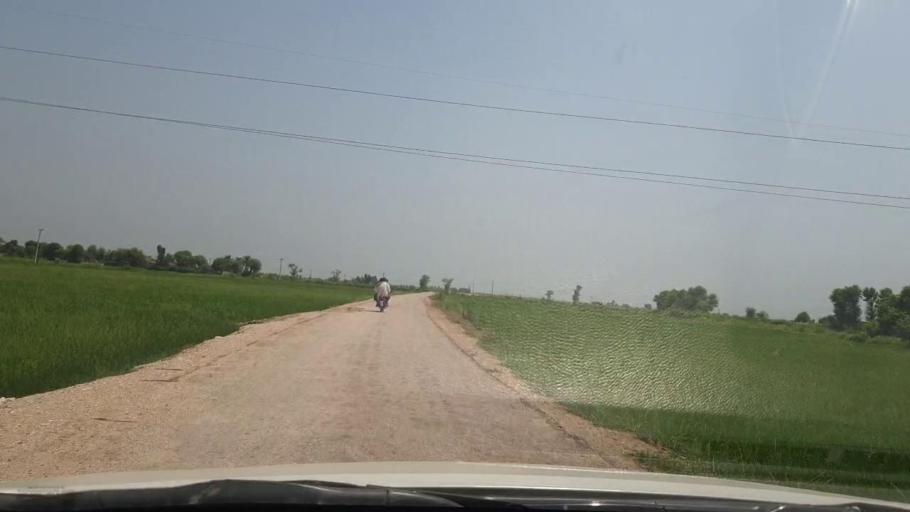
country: PK
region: Sindh
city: Rustam jo Goth
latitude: 28.0224
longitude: 68.8002
